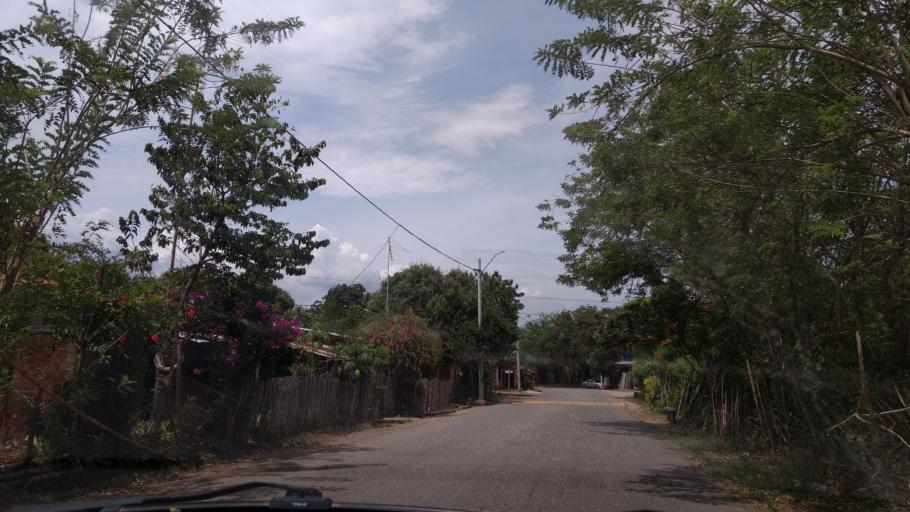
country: CO
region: Cauca
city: Buenos Aires
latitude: 3.0499
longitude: -76.6569
